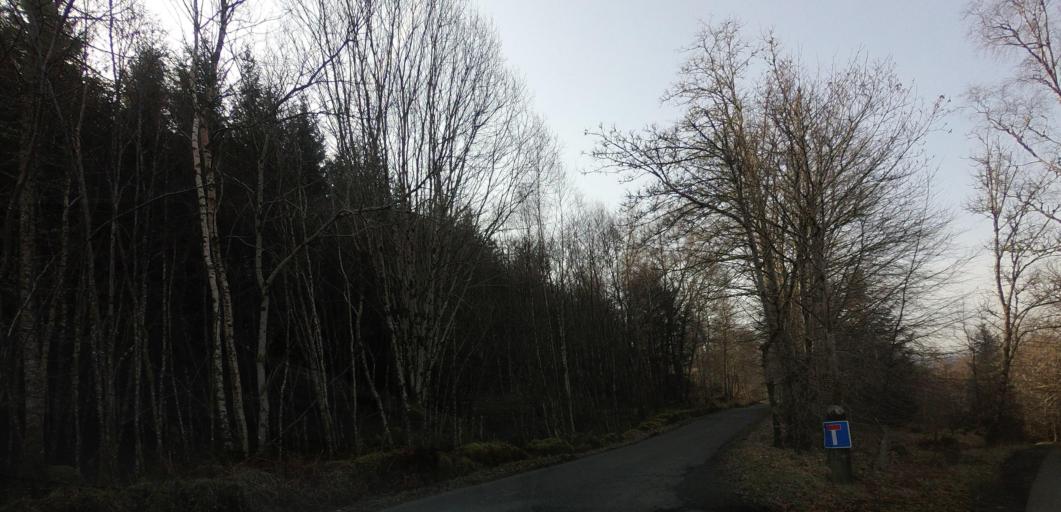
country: GB
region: Scotland
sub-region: Stirling
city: Callander
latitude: 56.4666
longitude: -4.2891
